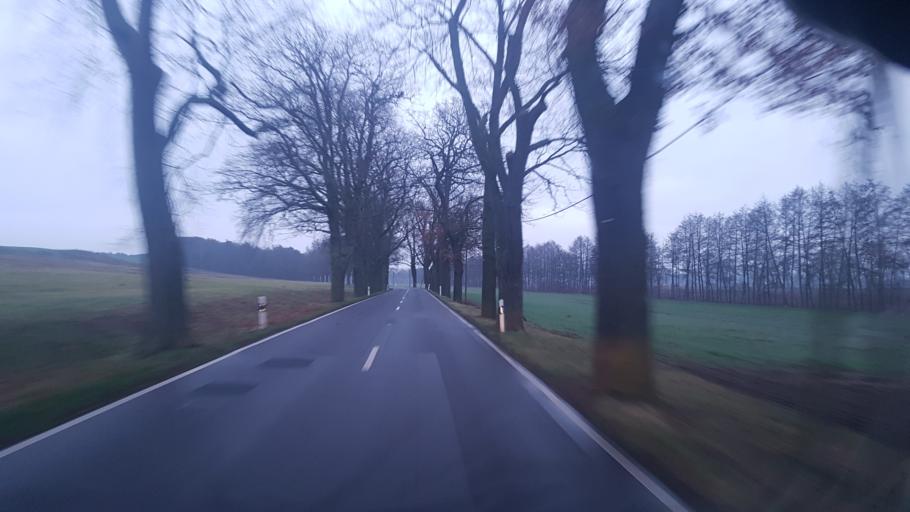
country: DE
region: Brandenburg
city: Trebbin
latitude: 52.2433
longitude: 13.2172
